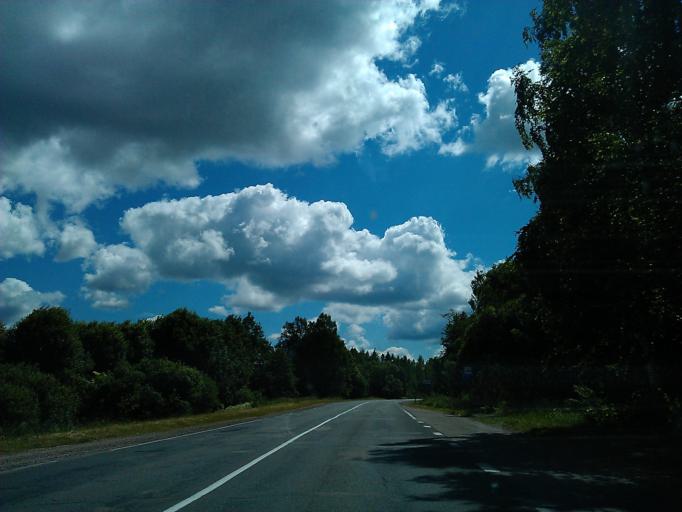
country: LV
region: Varaklani
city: Varaklani
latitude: 56.6092
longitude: 26.8409
